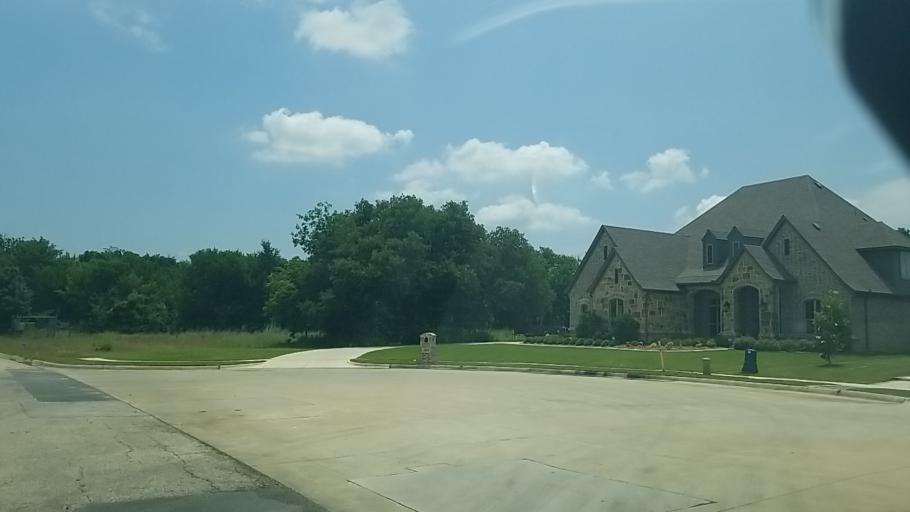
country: US
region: Texas
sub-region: Denton County
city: Corinth
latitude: 33.1636
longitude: -97.0853
